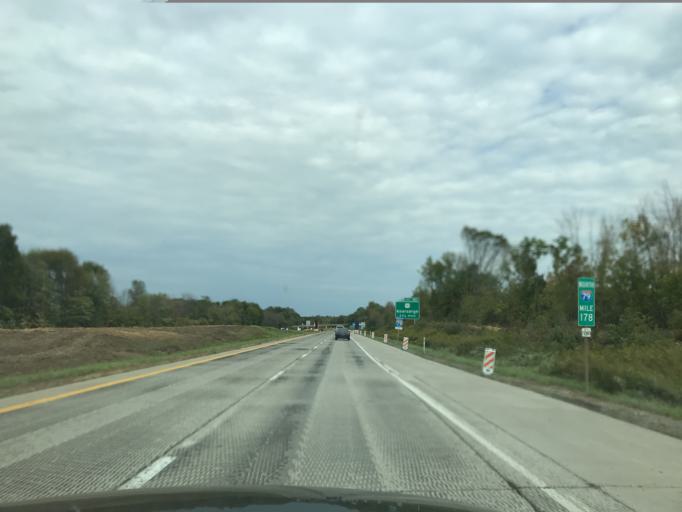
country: US
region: Pennsylvania
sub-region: Erie County
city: Erie
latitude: 42.0400
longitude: -80.1202
